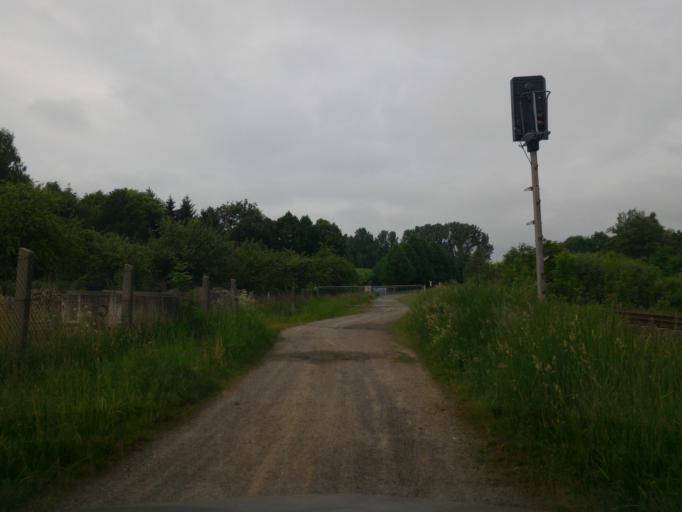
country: DE
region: Saxony
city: Leutersdorf
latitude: 50.9504
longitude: 14.6538
